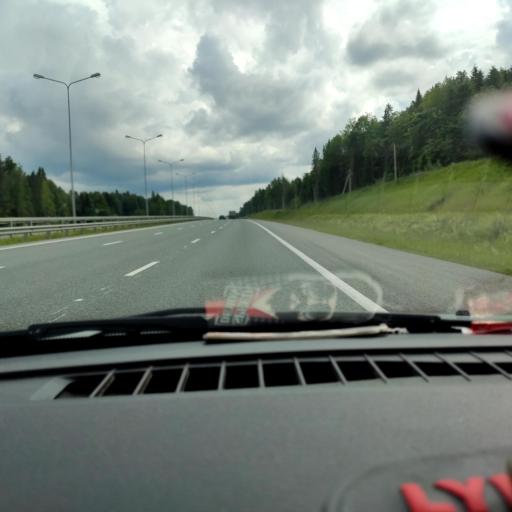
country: RU
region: Perm
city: Zvezdnyy
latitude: 57.7611
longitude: 56.3325
